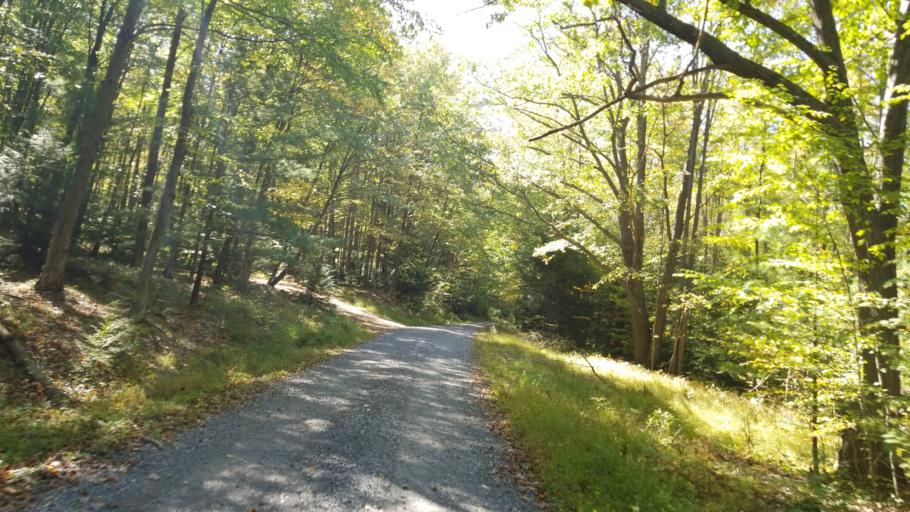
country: US
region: Pennsylvania
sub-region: Clearfield County
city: Clearfield
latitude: 41.1866
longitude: -78.5057
